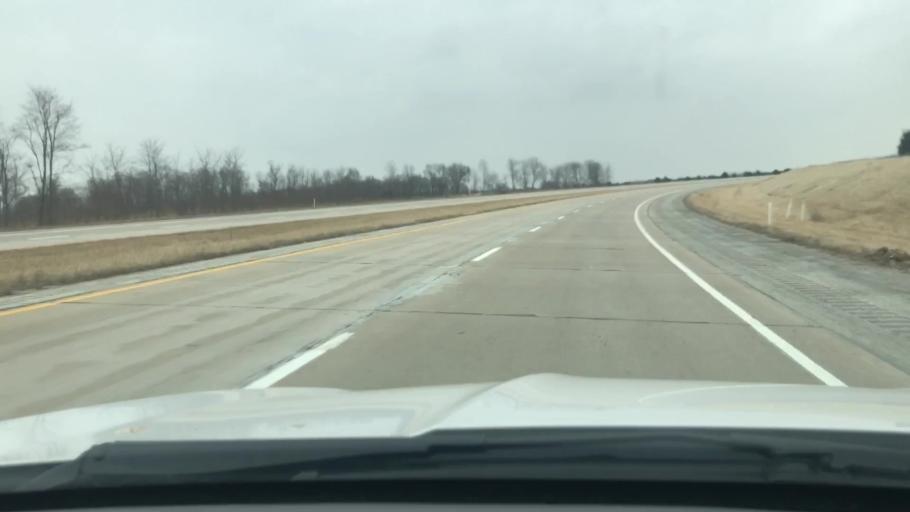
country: US
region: Indiana
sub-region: Cass County
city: Logansport
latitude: 40.7352
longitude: -86.3010
